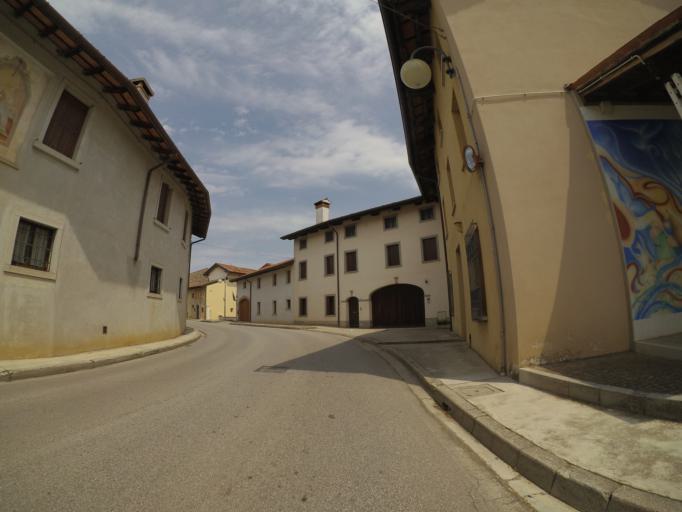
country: IT
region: Friuli Venezia Giulia
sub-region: Provincia di Udine
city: Sedegliano
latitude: 45.9998
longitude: 12.9978
